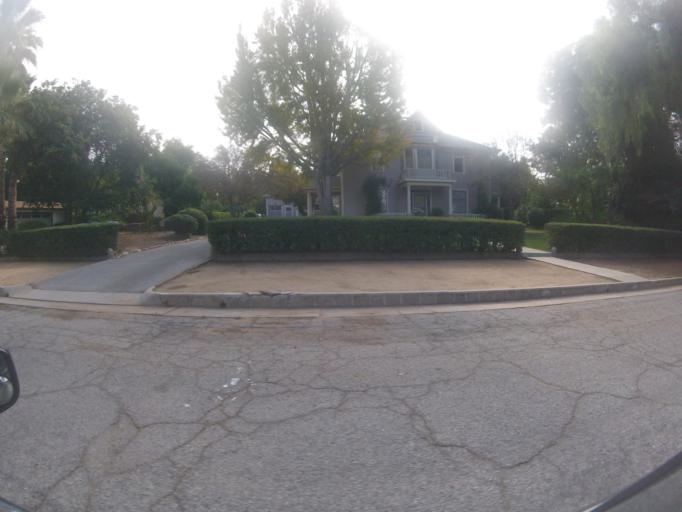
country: US
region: California
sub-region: San Bernardino County
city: Redlands
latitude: 34.0369
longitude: -117.1824
